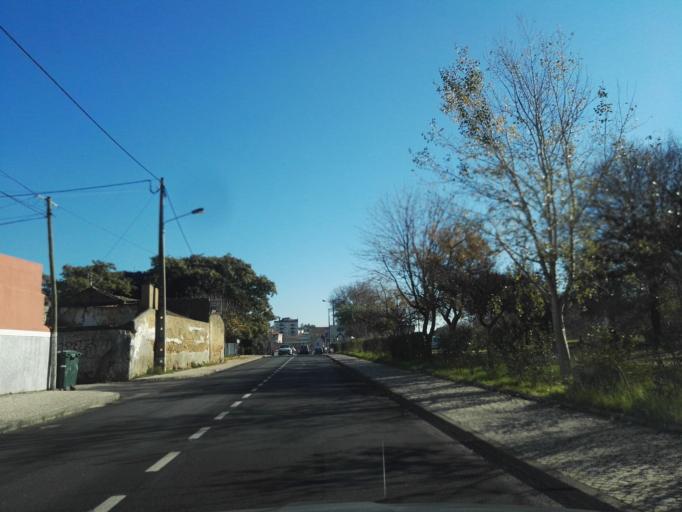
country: PT
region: Lisbon
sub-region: Vila Franca de Xira
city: Alhandra
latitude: 38.9305
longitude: -9.0150
